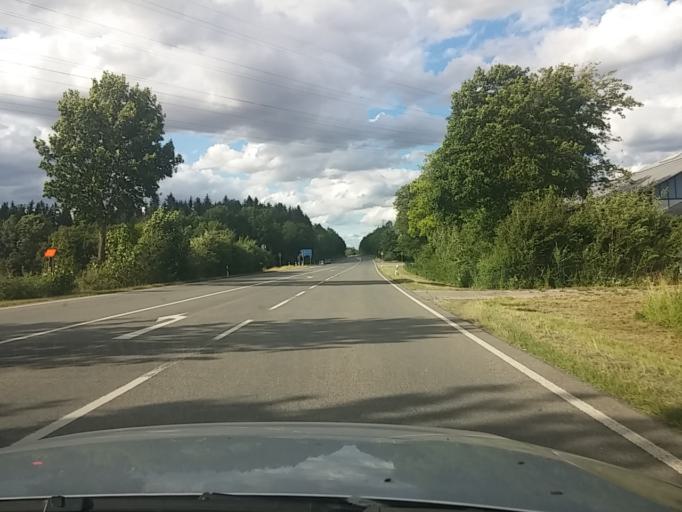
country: DE
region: Bavaria
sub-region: Upper Bavaria
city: Hohenbrunn
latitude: 48.0589
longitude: 11.7071
